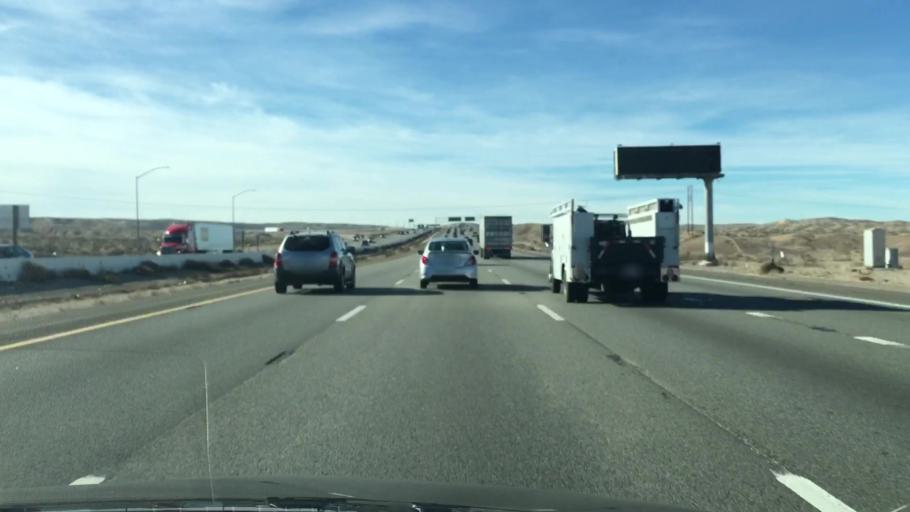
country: US
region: California
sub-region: San Bernardino County
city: Barstow Heights
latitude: 34.8794
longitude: -117.0670
